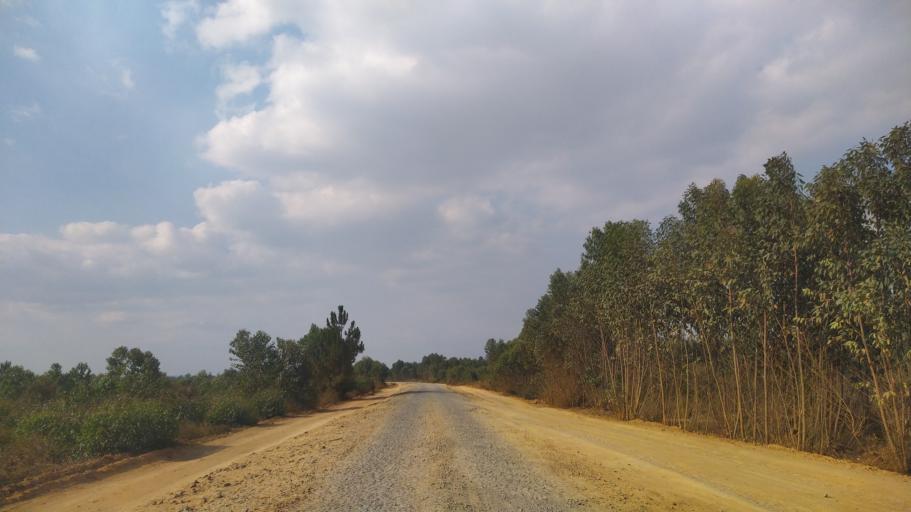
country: MG
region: Alaotra Mangoro
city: Moramanga
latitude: -18.6453
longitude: 48.2752
